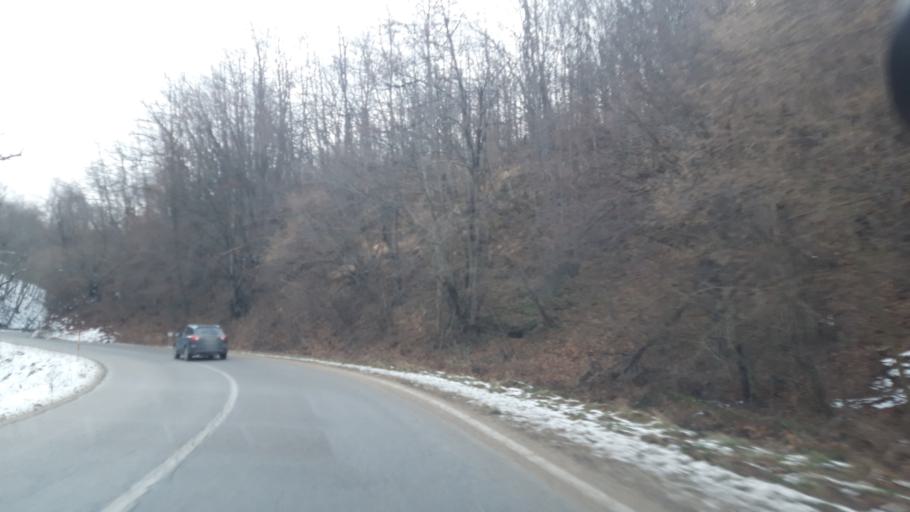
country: BA
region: Republika Srpska
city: Vlasenica
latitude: 44.1828
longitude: 19.0074
